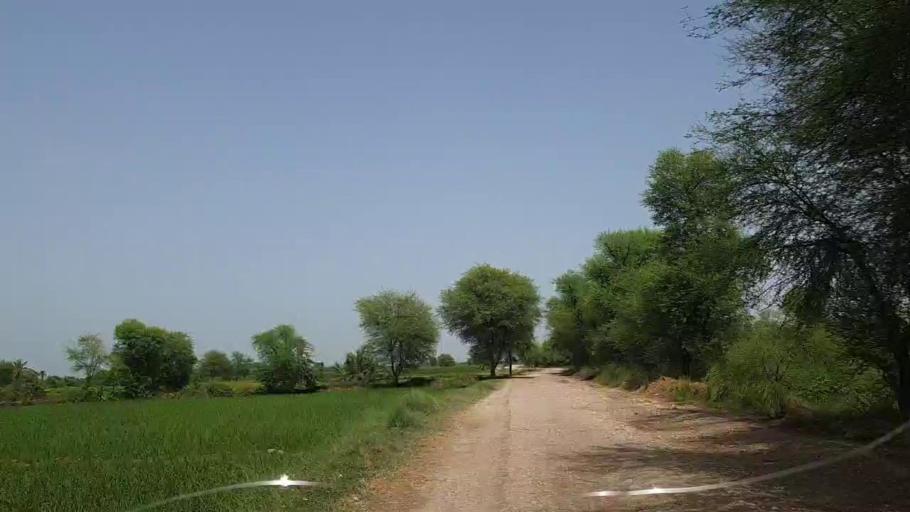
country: PK
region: Sindh
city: Kandiaro
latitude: 27.0143
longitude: 68.1582
